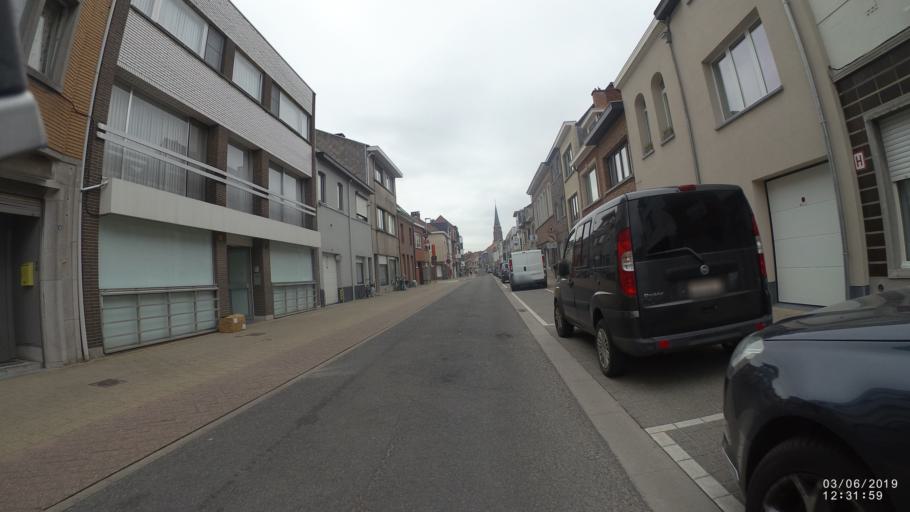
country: BE
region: Flanders
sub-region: Provincie Oost-Vlaanderen
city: Sint-Niklaas
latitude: 51.1593
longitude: 4.1441
